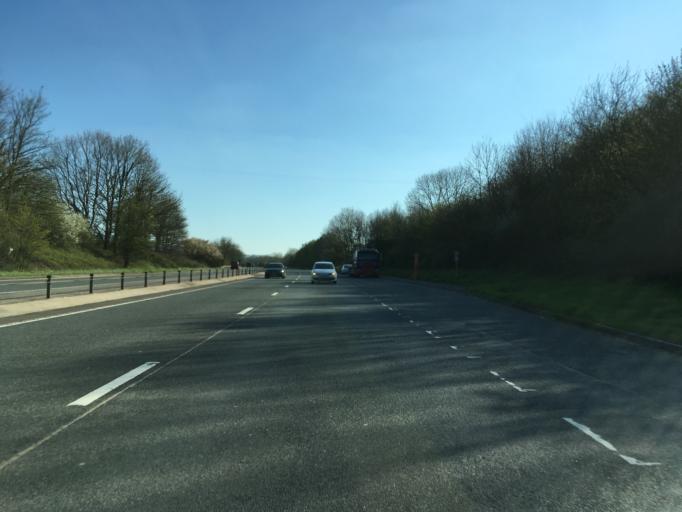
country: GB
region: Wales
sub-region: Monmouthshire
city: Llanbadoc
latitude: 51.6968
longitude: -2.8788
